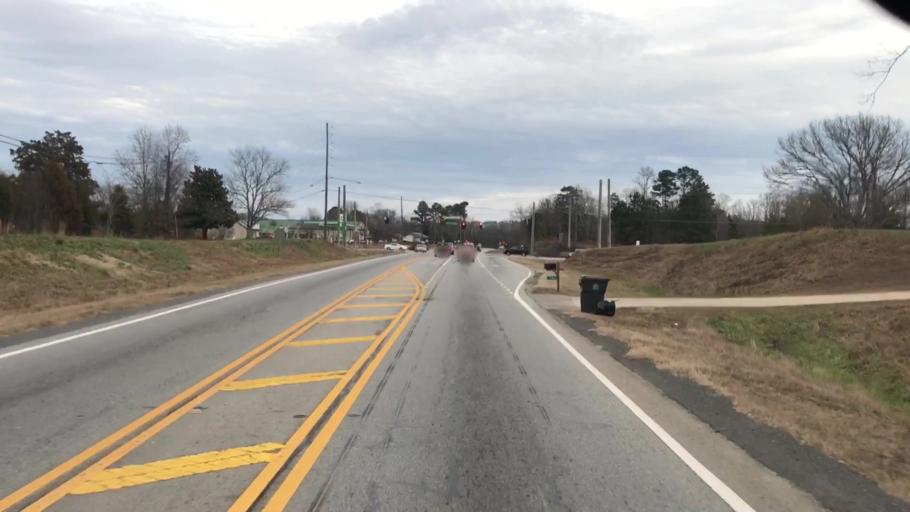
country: US
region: Georgia
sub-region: Barrow County
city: Winder
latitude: 34.0230
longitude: -83.7666
